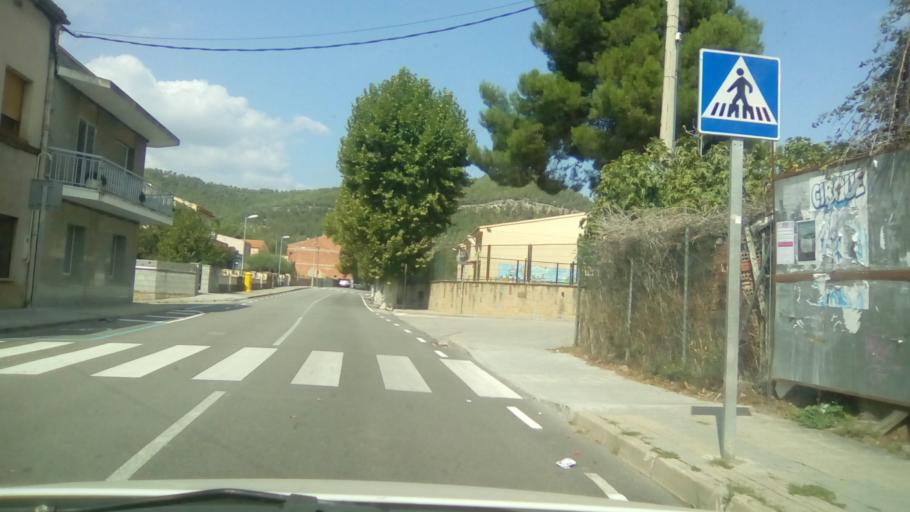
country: ES
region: Catalonia
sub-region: Provincia de Barcelona
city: Monistrol de Montserrat
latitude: 41.6319
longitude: 1.8542
